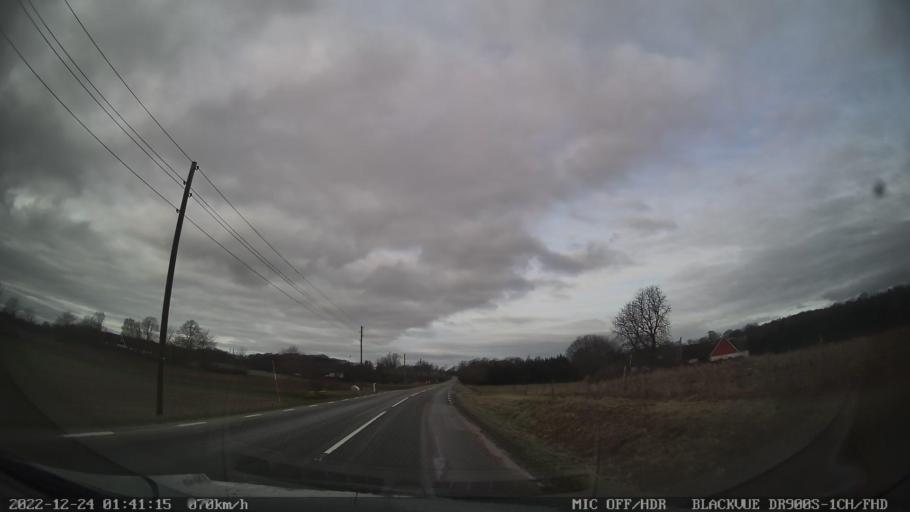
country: SE
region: Skane
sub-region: Tomelilla Kommun
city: Tomelilla
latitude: 55.5923
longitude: 14.0921
